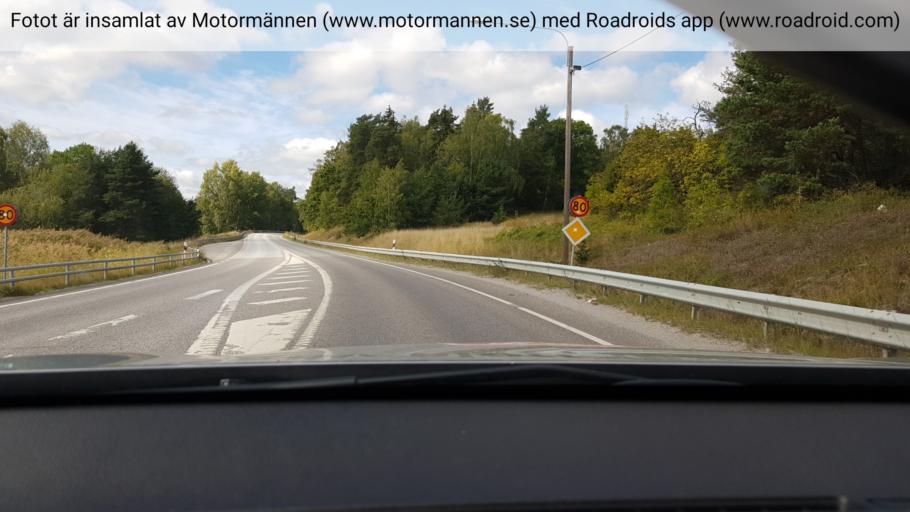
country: SE
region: Stockholm
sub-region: Vaxholms Kommun
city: Resaro
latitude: 59.4174
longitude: 18.3092
